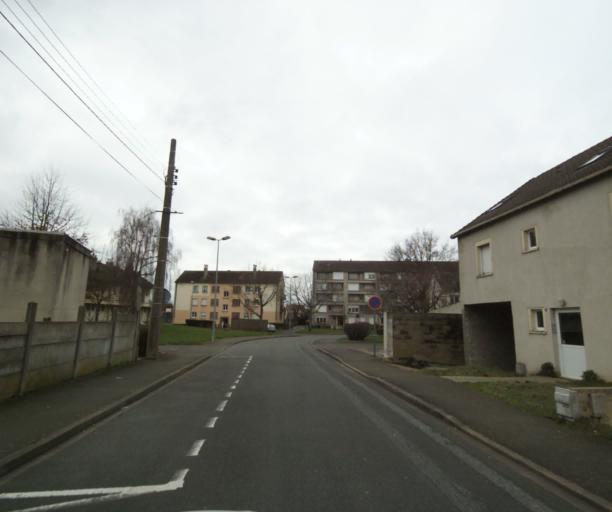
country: FR
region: Pays de la Loire
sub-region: Departement de la Sarthe
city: Le Mans
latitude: 47.9762
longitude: 0.2066
